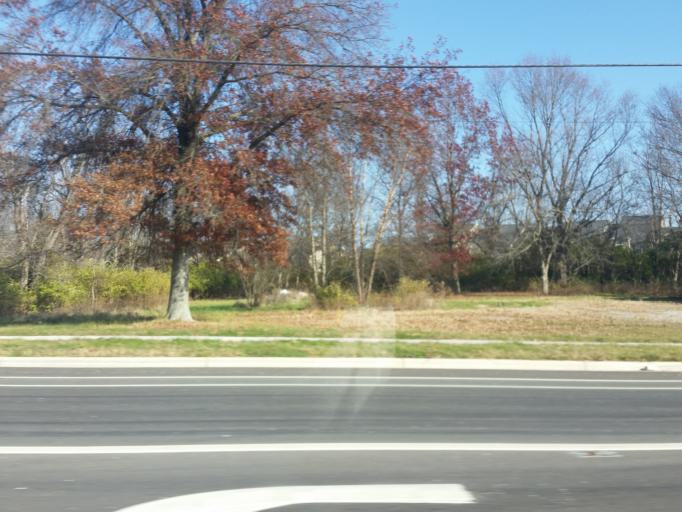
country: US
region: Ohio
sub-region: Butler County
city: Oxford
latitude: 39.4908
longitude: -84.7228
